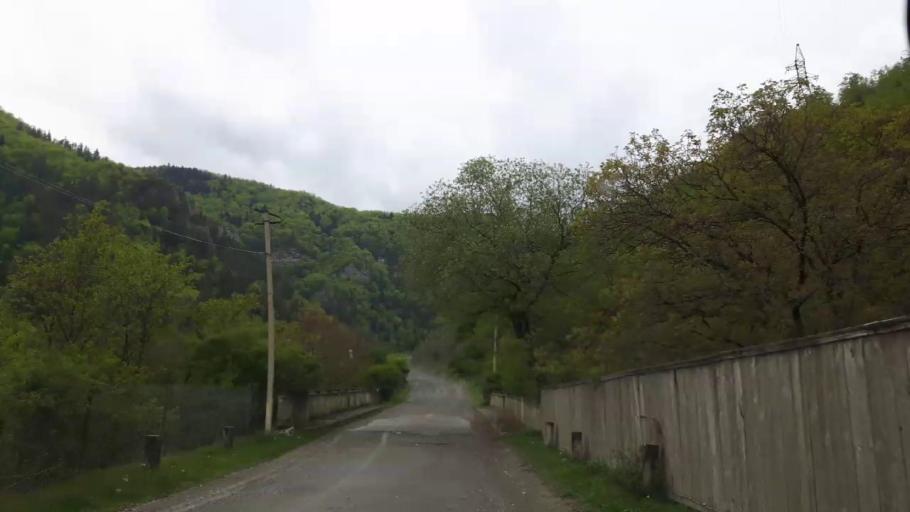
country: GE
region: Shida Kartli
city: Gori
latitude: 41.8674
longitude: 43.9824
